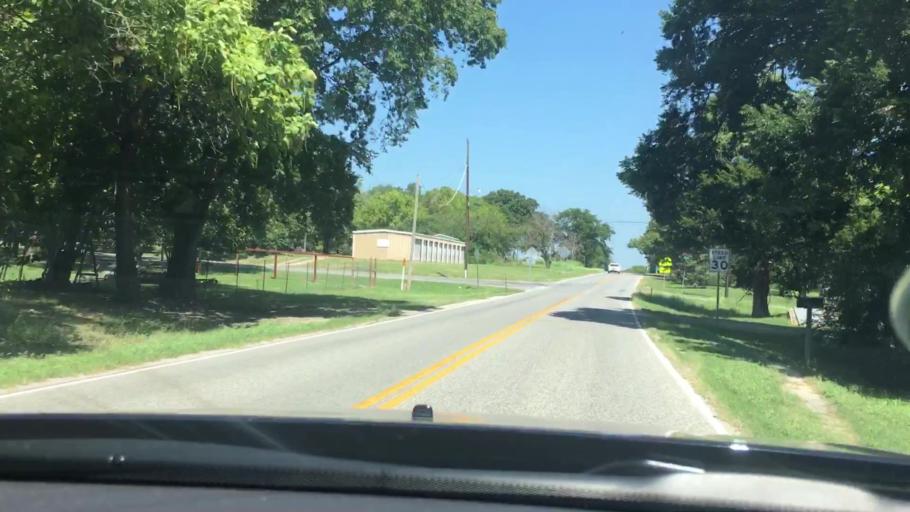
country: US
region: Oklahoma
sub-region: Johnston County
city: Tishomingo
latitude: 34.2409
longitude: -96.5486
